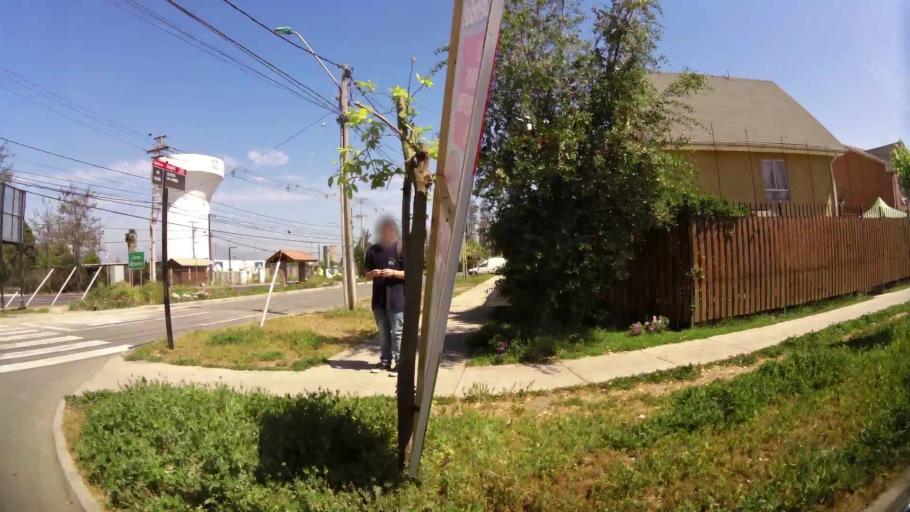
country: CL
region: Santiago Metropolitan
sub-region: Provincia de Talagante
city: Talagante
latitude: -33.6532
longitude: -70.8995
